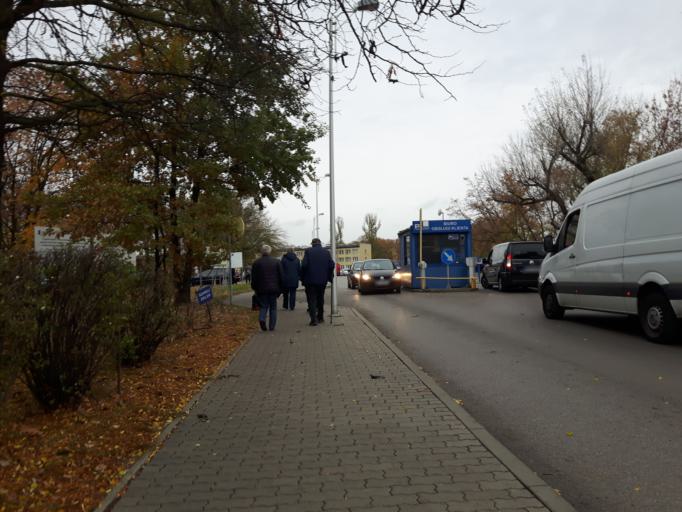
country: PL
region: Masovian Voivodeship
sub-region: Warszawa
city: Praga Poludnie
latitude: 52.2505
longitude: 21.0888
